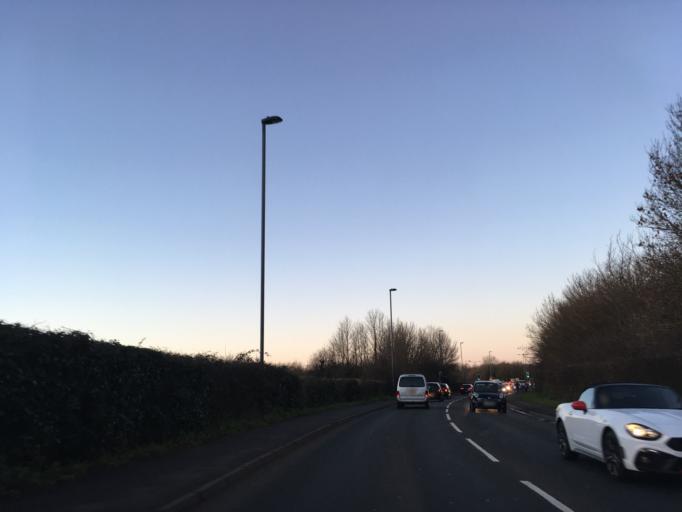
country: GB
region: England
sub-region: South Gloucestershire
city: Stoke Gifford
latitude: 51.5196
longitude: -2.5501
